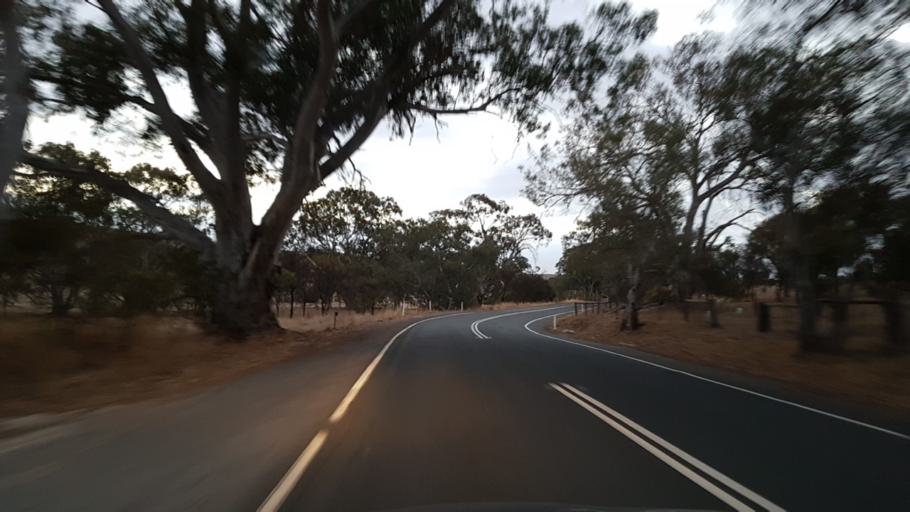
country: AU
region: South Australia
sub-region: Mount Barker
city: Nairne
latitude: -35.0327
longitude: 138.9716
